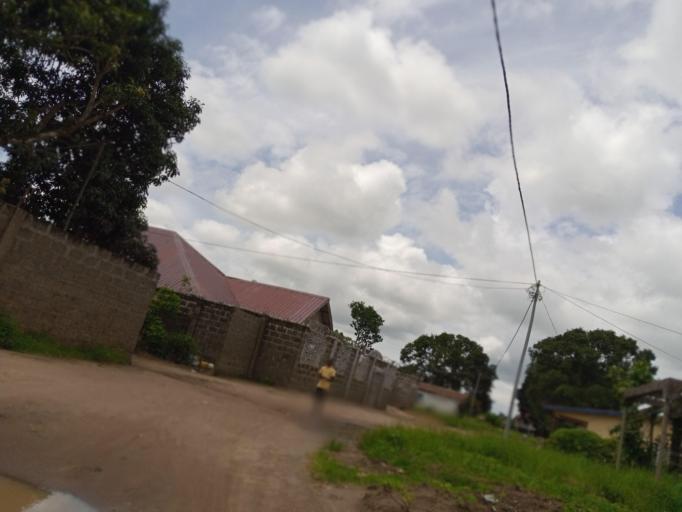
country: SL
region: Northern Province
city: Masoyila
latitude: 8.6033
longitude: -13.1852
